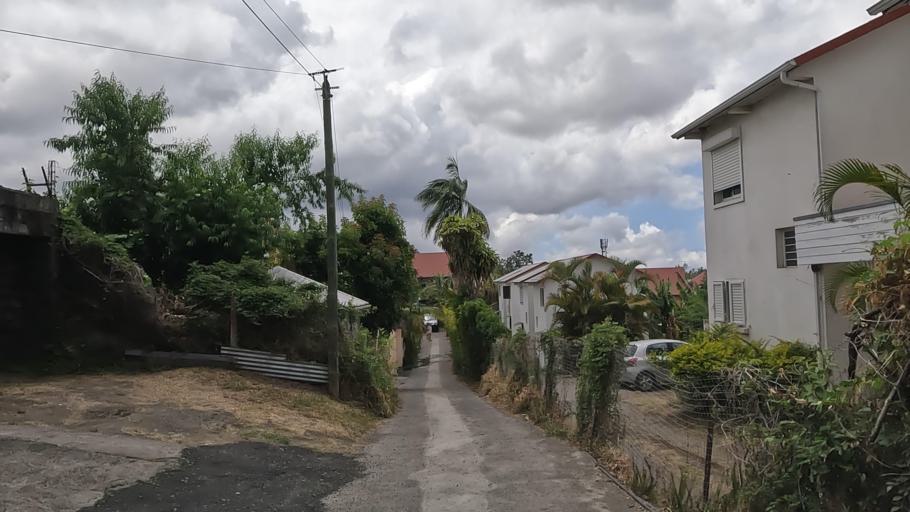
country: RE
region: Reunion
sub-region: Reunion
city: Le Tampon
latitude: -21.2650
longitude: 55.5172
